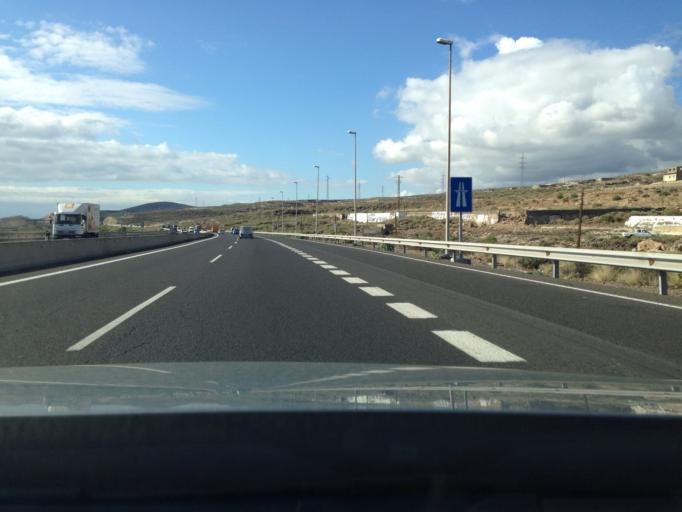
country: ES
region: Canary Islands
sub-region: Provincia de Santa Cruz de Tenerife
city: Fasnia
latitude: 28.2122
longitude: -16.4236
